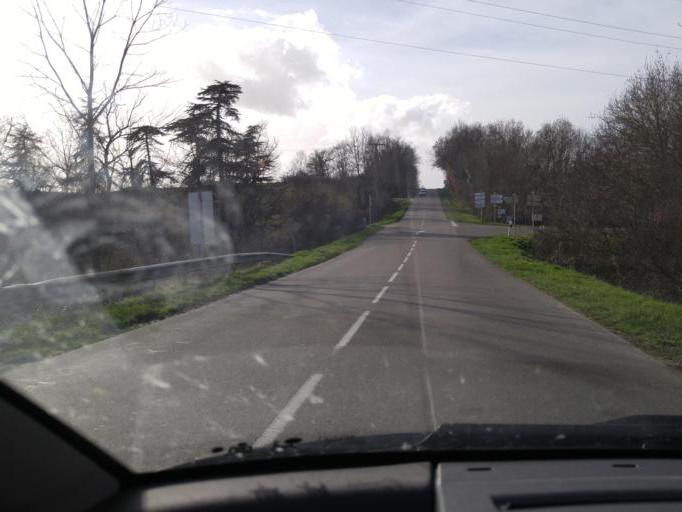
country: FR
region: Midi-Pyrenees
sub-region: Departement du Gers
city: Lectoure
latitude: 43.9347
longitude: 0.6047
